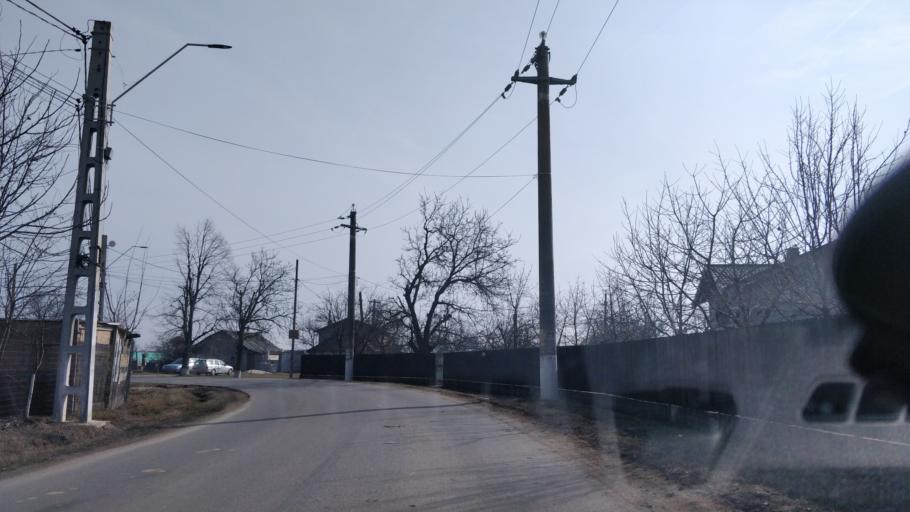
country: RO
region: Giurgiu
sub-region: Comuna Bolintin Deal
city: Bolintin Deal
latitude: 44.4805
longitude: 25.8069
